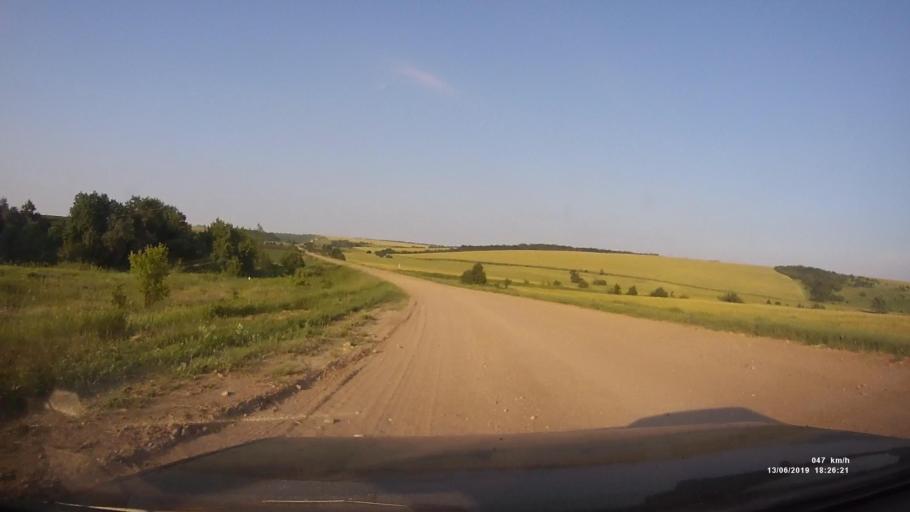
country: RU
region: Rostov
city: Kazanskaya
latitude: 49.8504
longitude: 41.3113
